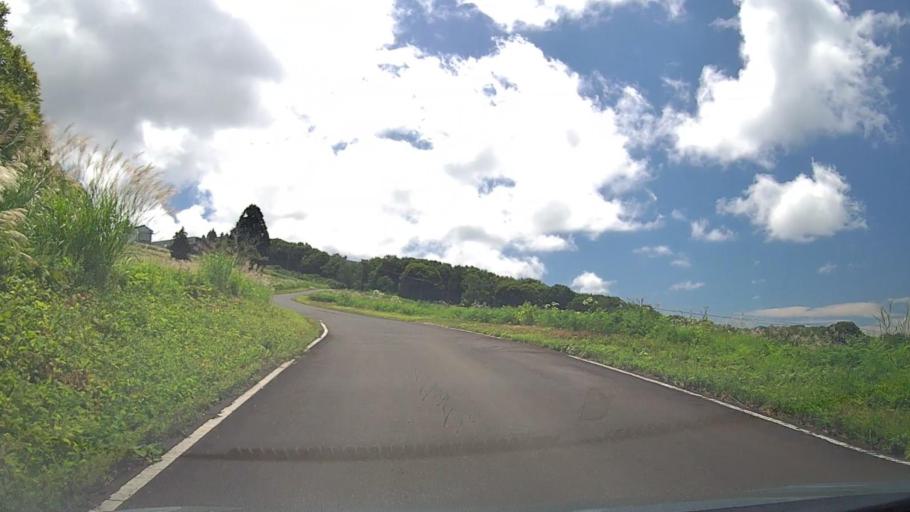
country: JP
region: Nagano
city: Iiyama
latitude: 36.9248
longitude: 138.4745
